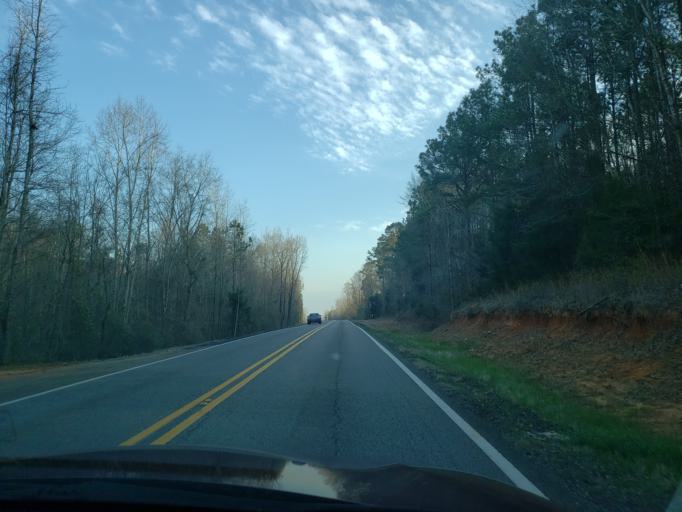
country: US
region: Alabama
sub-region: Hale County
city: Greensboro
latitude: 32.7857
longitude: -87.5892
